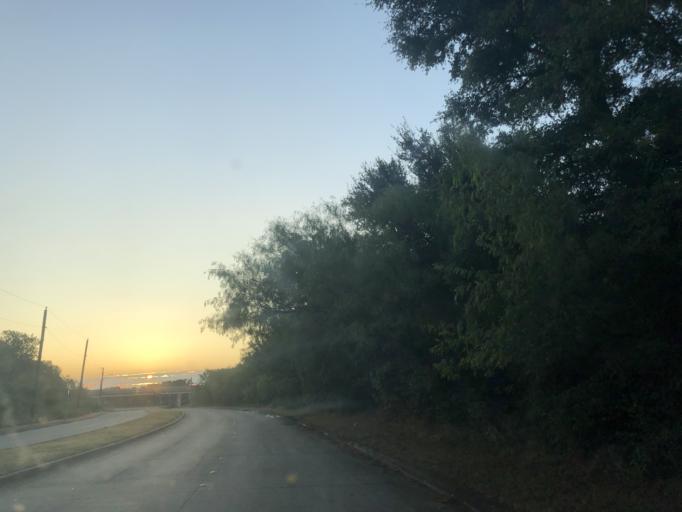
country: US
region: Texas
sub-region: Tarrant County
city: Euless
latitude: 32.8450
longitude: -97.0652
